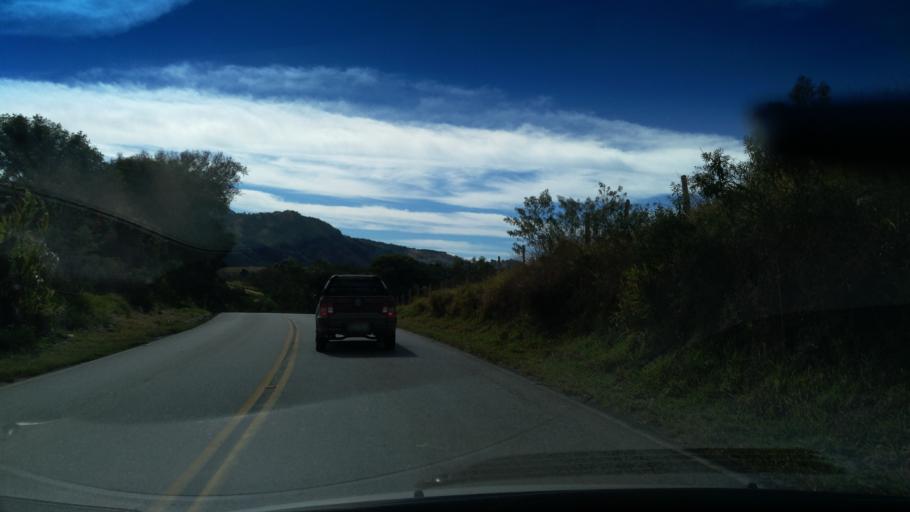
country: BR
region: Minas Gerais
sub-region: Andradas
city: Andradas
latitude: -22.0687
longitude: -46.4415
